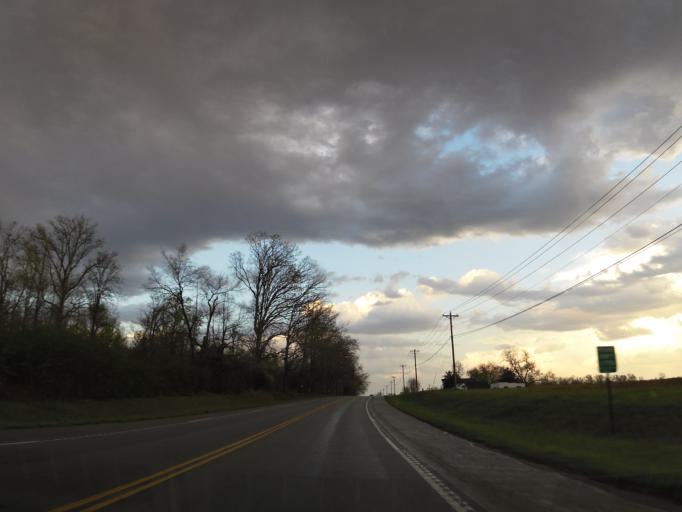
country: US
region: Tennessee
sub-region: DeKalb County
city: Smithville
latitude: 35.9704
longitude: -85.8073
